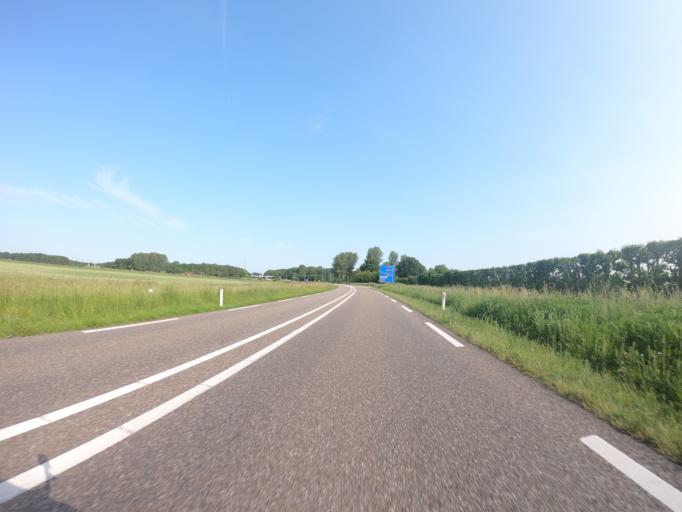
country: NL
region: North Brabant
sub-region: Gemeente Landerd
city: Reek
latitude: 51.7849
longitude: 5.6642
